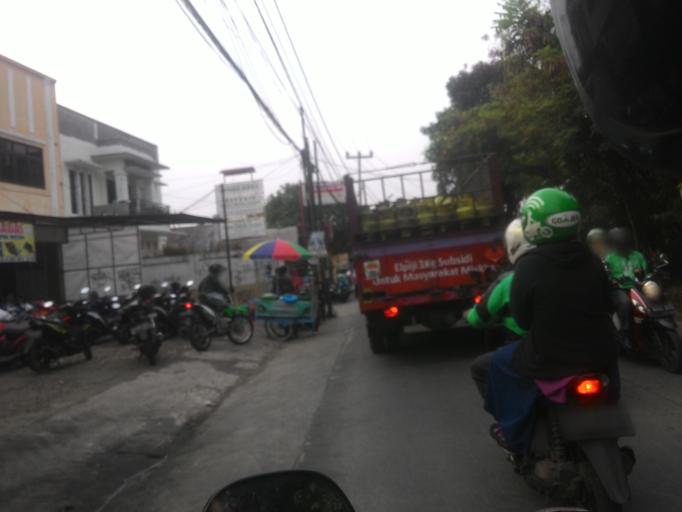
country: ID
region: West Java
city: Depok
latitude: -6.3713
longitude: 106.8132
